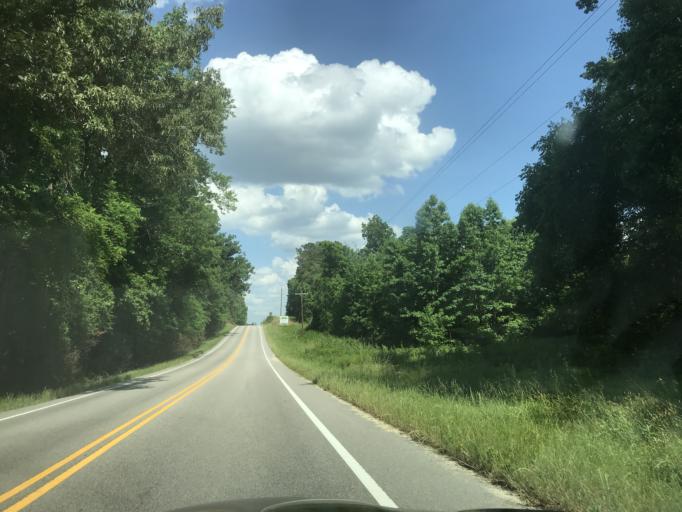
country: US
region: North Carolina
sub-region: Franklin County
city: Louisburg
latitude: 35.9627
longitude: -78.2971
